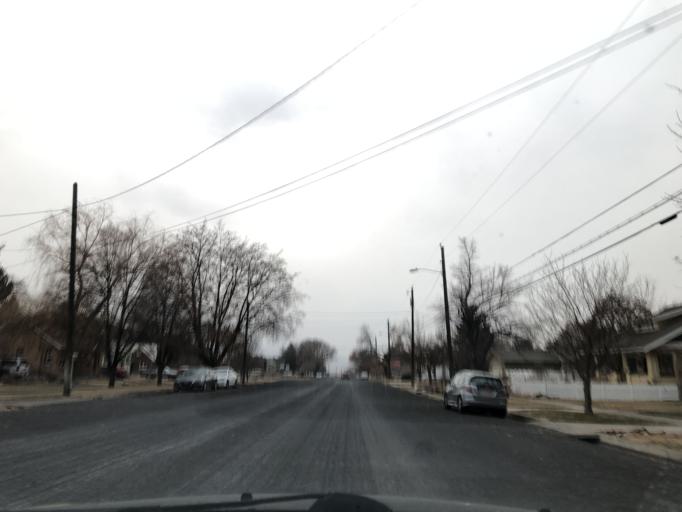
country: US
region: Utah
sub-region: Cache County
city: Logan
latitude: 41.7335
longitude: -111.8439
